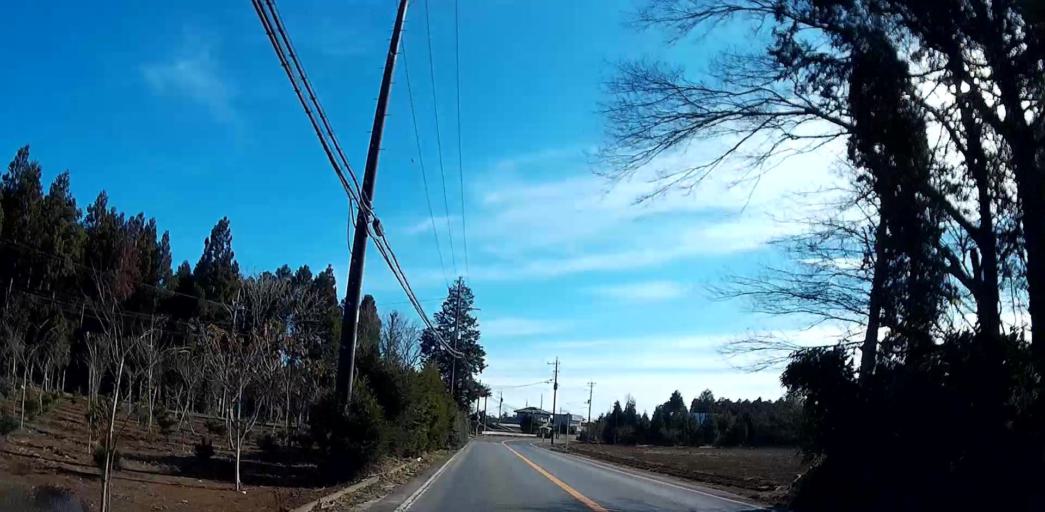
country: JP
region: Chiba
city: Yokaichiba
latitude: 35.7657
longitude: 140.4448
